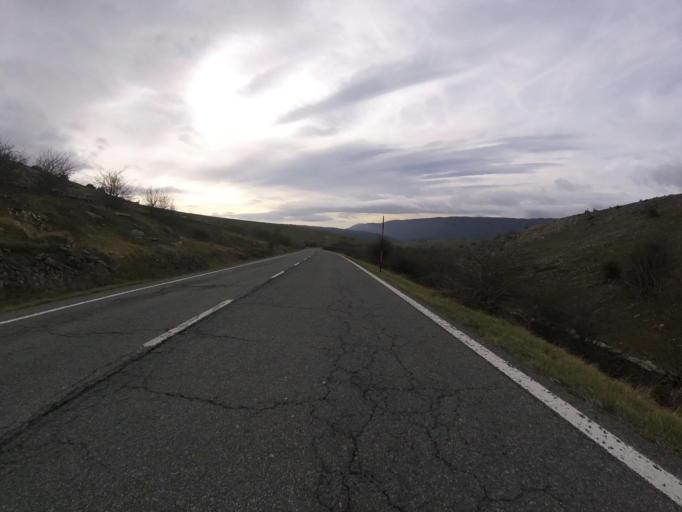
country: ES
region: Navarre
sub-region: Provincia de Navarra
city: Arbizu
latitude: 42.8567
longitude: -2.0130
